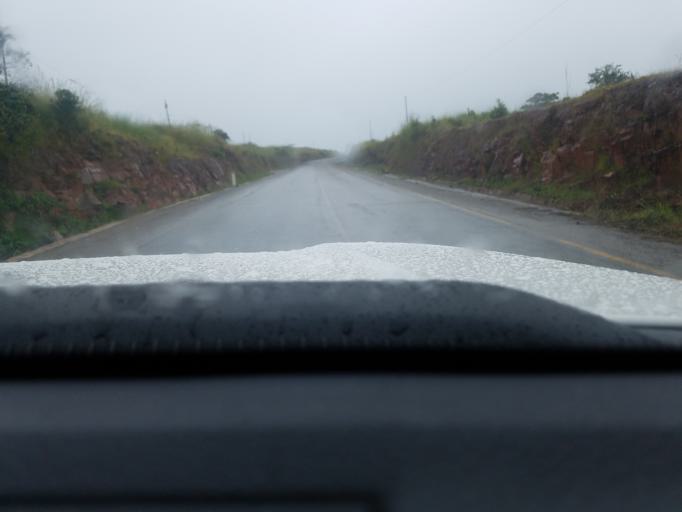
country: TZ
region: Kigoma
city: Mwandiga
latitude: -4.6640
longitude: 29.7244
